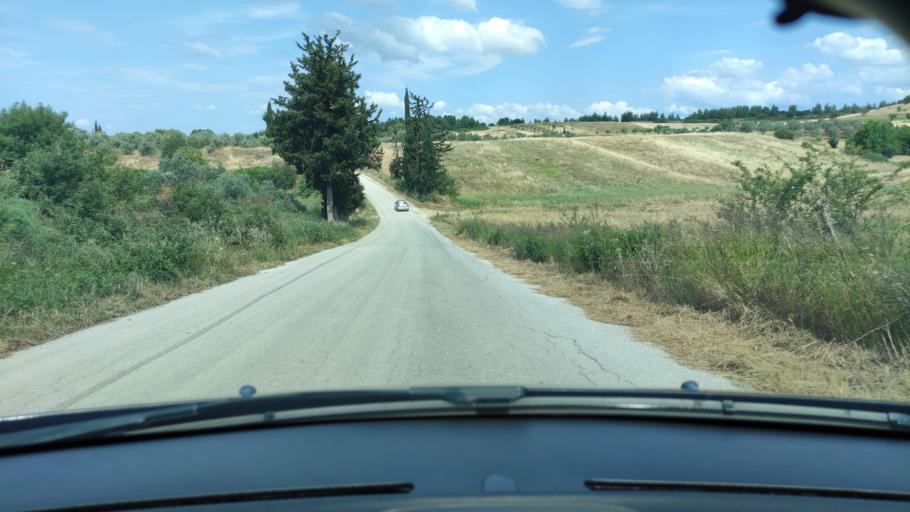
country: GR
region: Central Greece
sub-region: Nomos Evvoias
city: Afration
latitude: 38.5184
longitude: 23.7663
